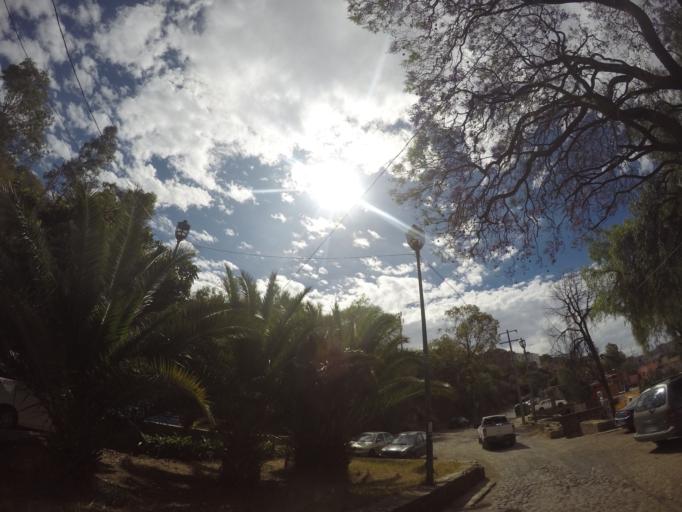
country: MX
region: Guanajuato
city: Guanajuato
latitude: 21.0145
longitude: -101.2569
